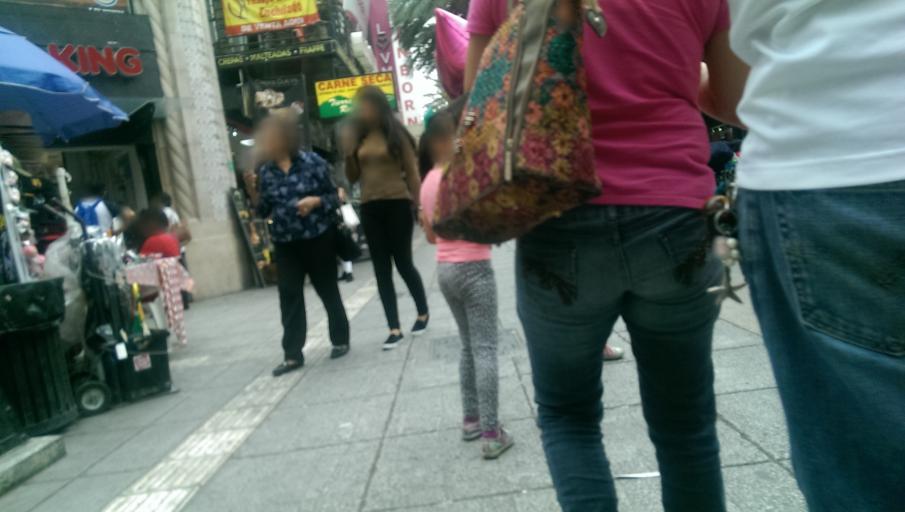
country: MX
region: Nuevo Leon
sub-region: Monterrey
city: Monterrey
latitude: 25.6672
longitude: -100.3116
